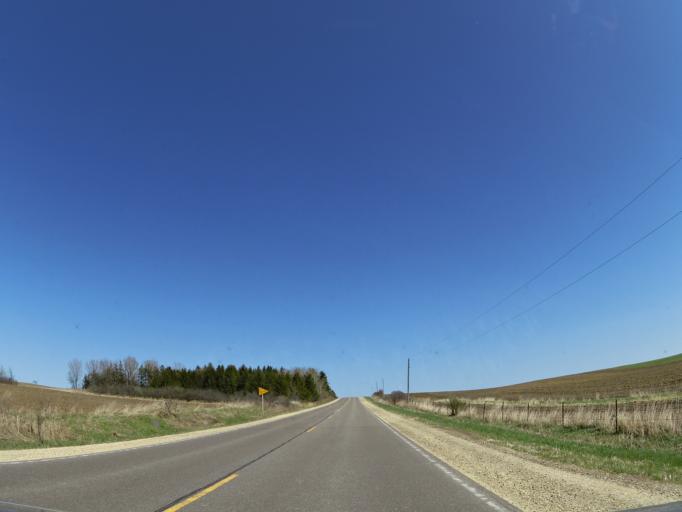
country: US
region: Wisconsin
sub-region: Saint Croix County
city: Hammond
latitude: 44.9344
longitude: -92.4625
